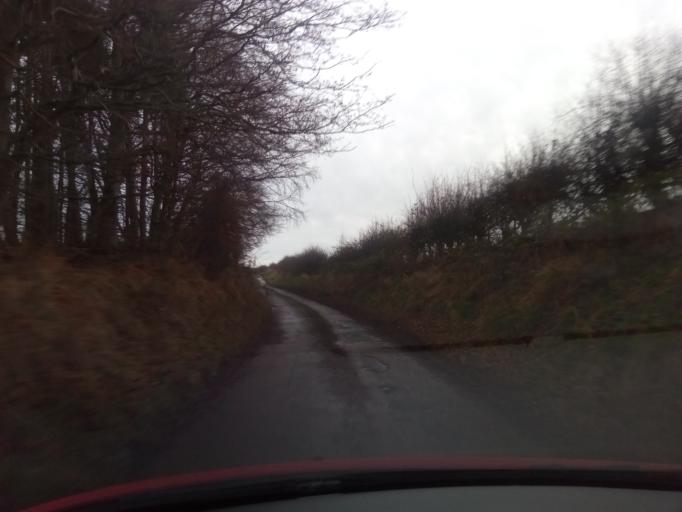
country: GB
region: England
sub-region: Northumberland
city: Whittingham
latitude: 55.4944
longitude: -1.9079
